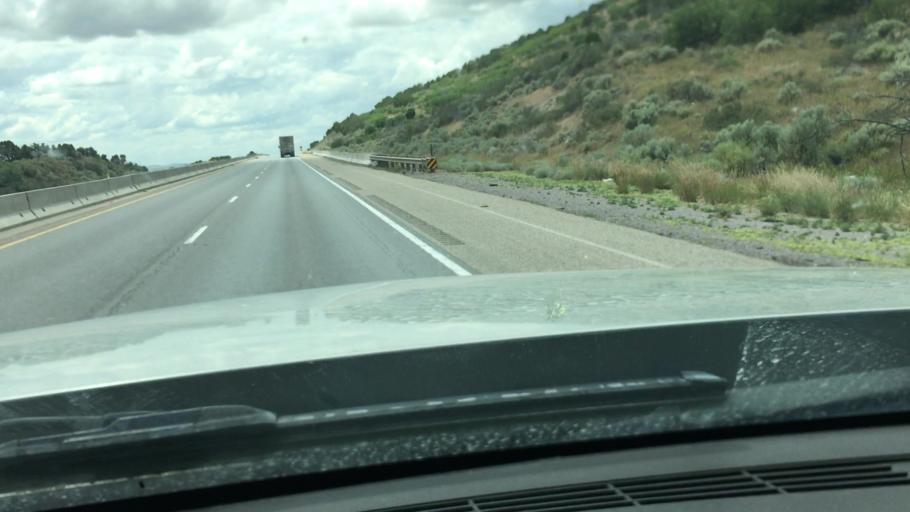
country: US
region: Utah
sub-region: Beaver County
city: Beaver
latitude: 38.4546
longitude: -112.6246
